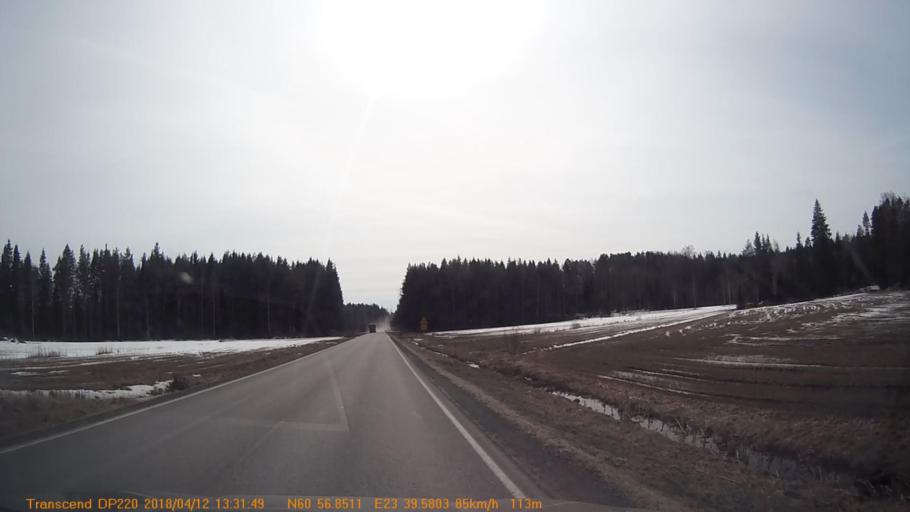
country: FI
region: Haeme
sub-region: Forssa
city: Forssa
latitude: 60.9474
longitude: 23.6596
